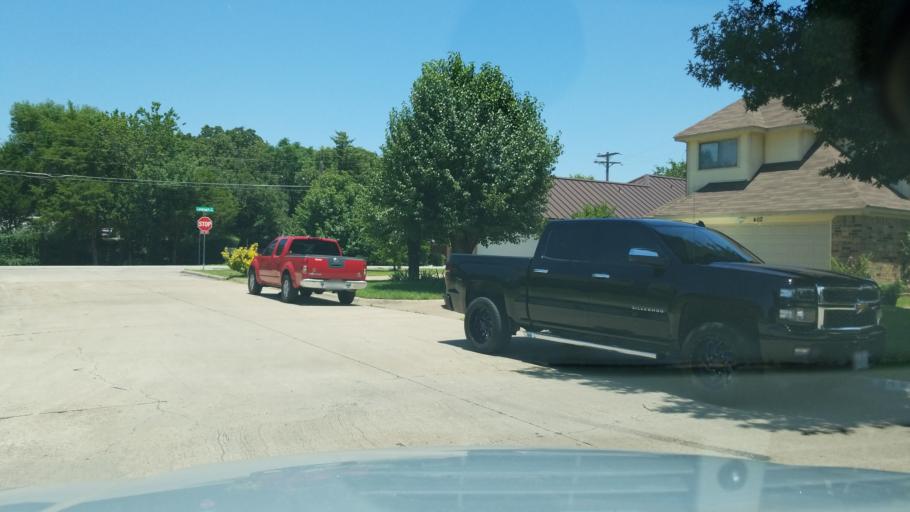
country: US
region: Texas
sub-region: Dallas County
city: Irving
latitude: 32.8108
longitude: -96.9242
